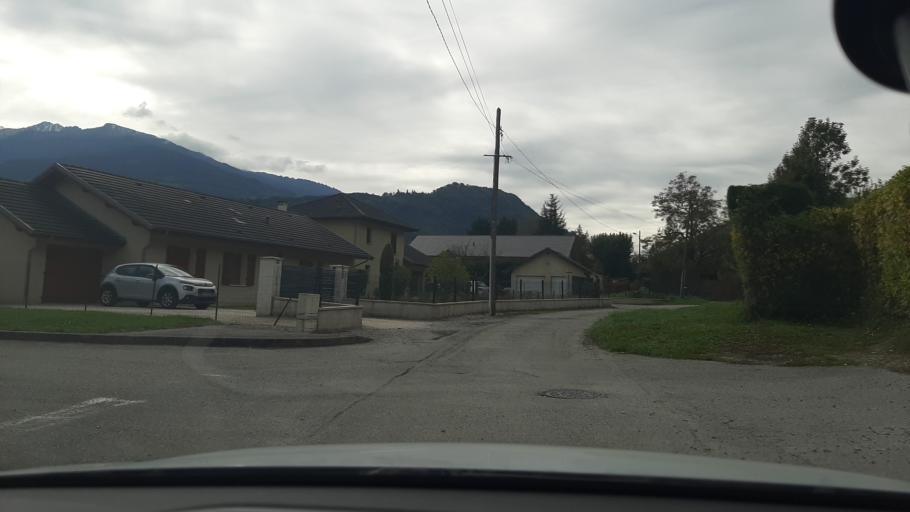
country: FR
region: Rhone-Alpes
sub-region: Departement de la Savoie
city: La Rochette
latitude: 45.4613
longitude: 6.1116
